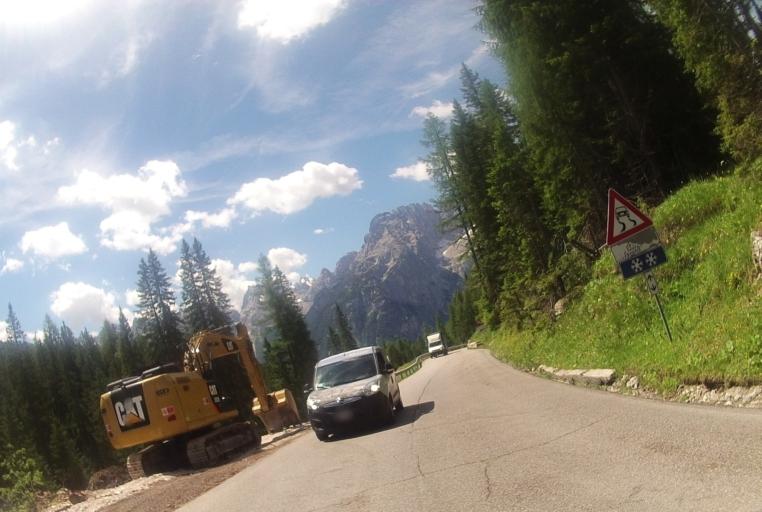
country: IT
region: Veneto
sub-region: Provincia di Belluno
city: Cortina d'Ampezzo
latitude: 46.5688
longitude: 12.2457
